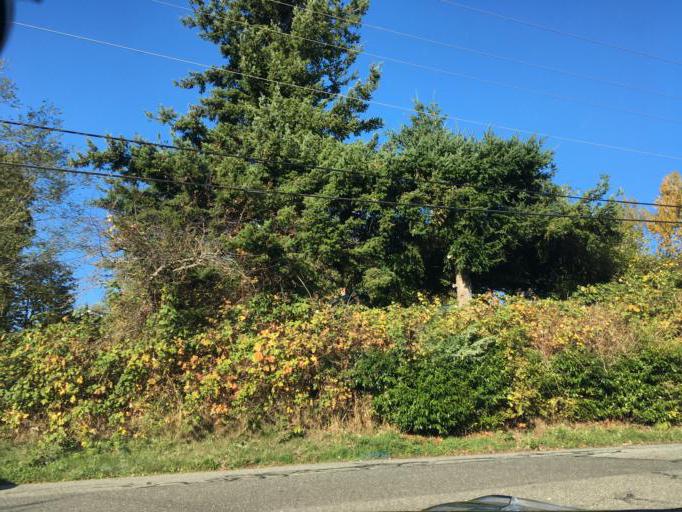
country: US
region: Washington
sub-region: Whatcom County
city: Bellingham
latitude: 48.7798
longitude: -122.5072
